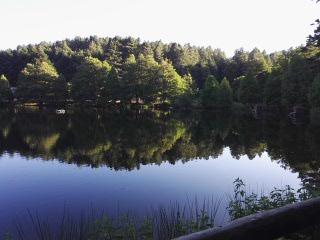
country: IT
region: Calabria
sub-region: Provincia di Vibo-Valentia
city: Mongiana
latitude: 38.5218
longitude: 16.3049
